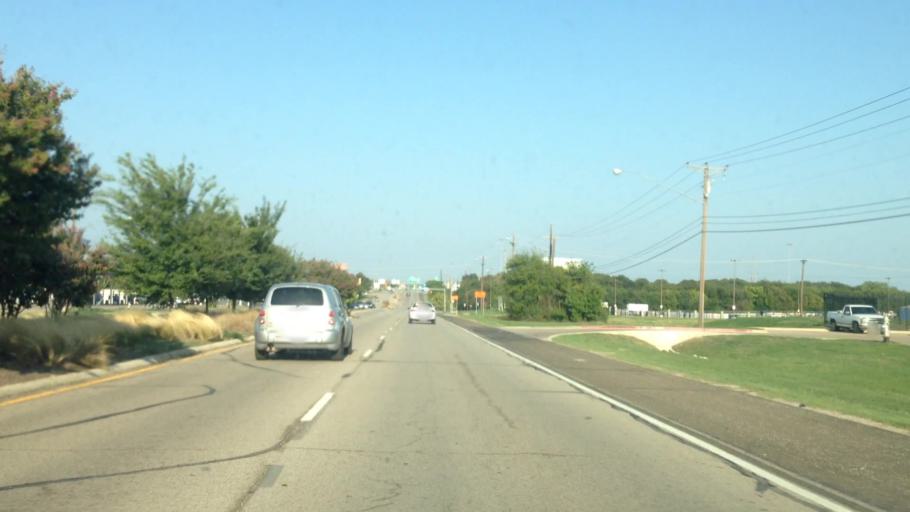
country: US
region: Texas
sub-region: Tarrant County
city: Richland Hills
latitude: 32.8090
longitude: -97.2184
